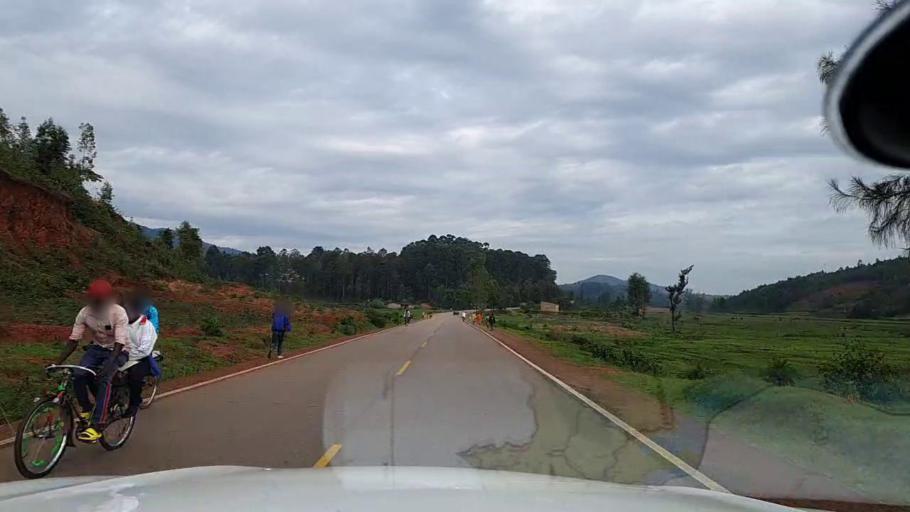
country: RW
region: Southern Province
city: Butare
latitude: -2.5663
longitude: 29.7263
